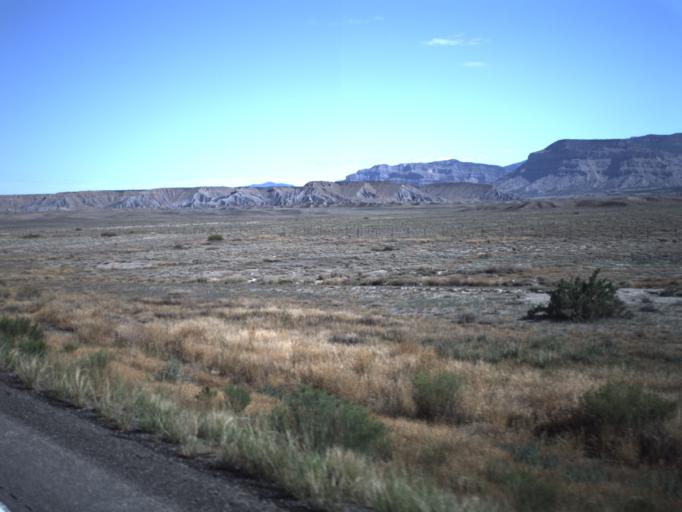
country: US
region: Utah
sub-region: Carbon County
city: East Carbon City
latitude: 39.3598
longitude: -110.3879
